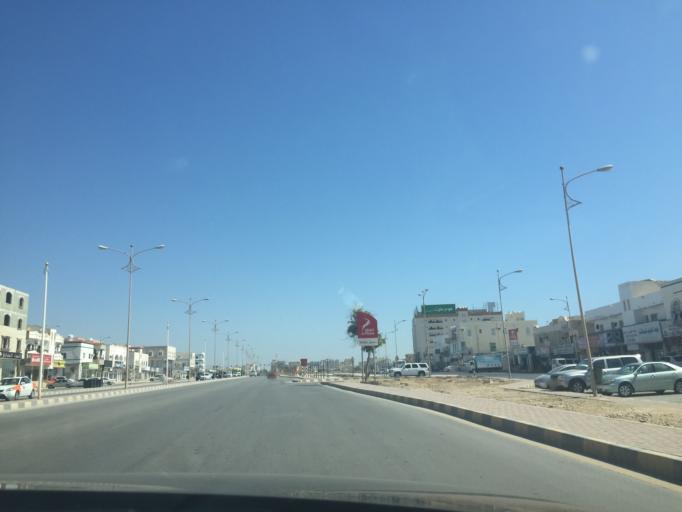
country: OM
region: Zufar
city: Salalah
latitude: 17.0078
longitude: 54.0698
